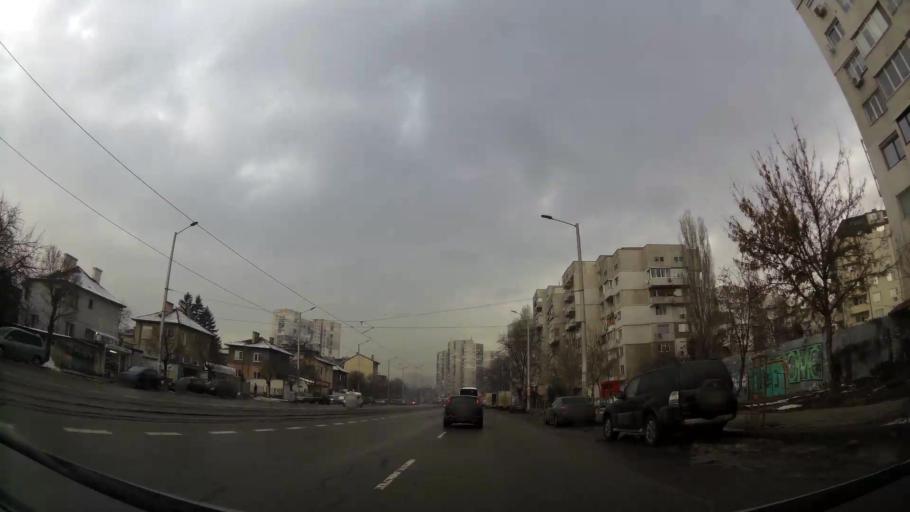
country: BG
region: Sofia-Capital
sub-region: Stolichna Obshtina
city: Sofia
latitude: 42.6951
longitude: 23.2905
